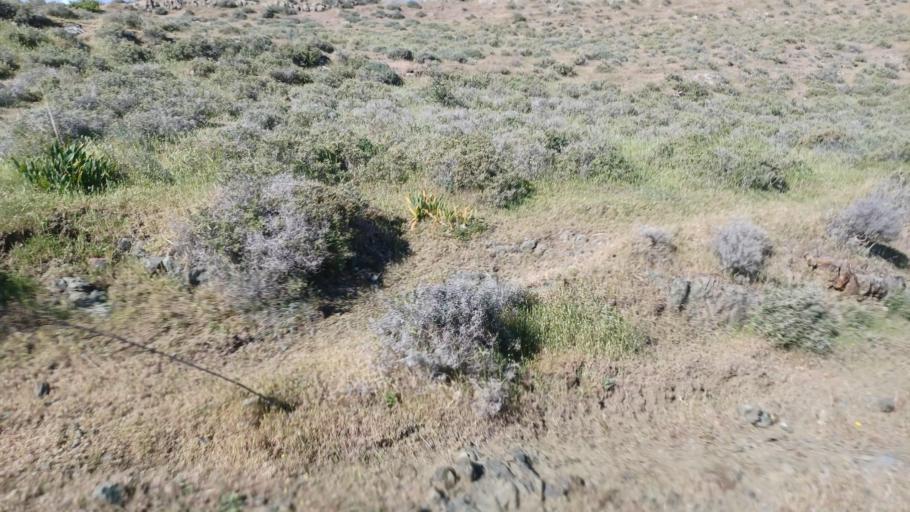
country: CY
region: Lefkosia
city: Peristerona
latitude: 35.0613
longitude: 33.0523
